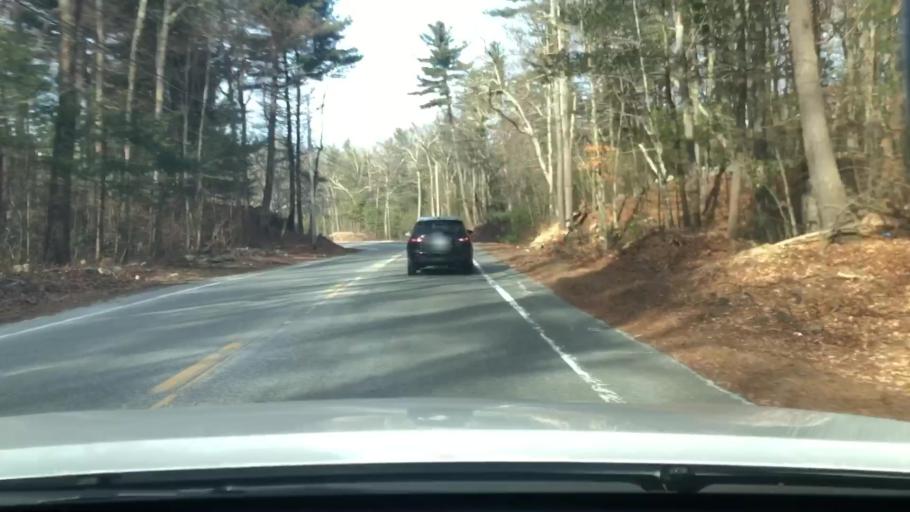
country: US
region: Massachusetts
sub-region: Worcester County
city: Grafton
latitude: 42.1984
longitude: -71.6568
